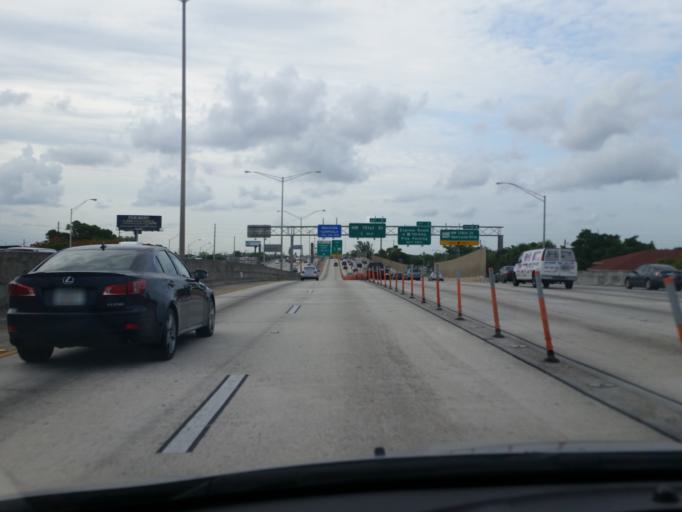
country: US
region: Florida
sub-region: Miami-Dade County
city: Golden Glades
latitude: 25.8946
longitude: -80.2095
